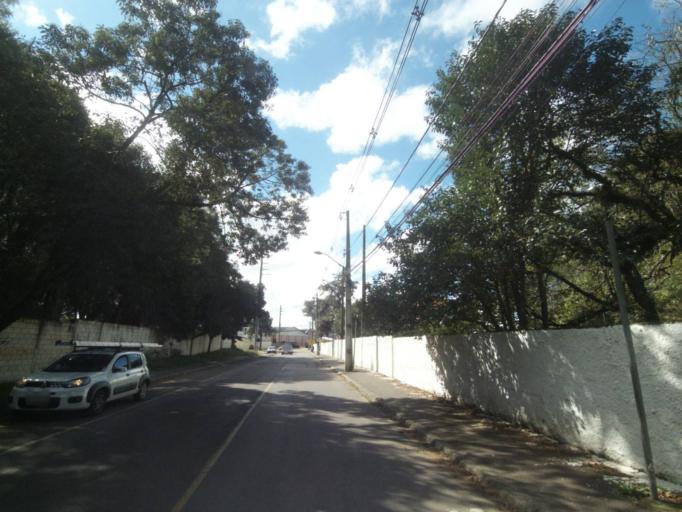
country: BR
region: Parana
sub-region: Sao Jose Dos Pinhais
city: Sao Jose dos Pinhais
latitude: -25.5330
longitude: -49.2921
